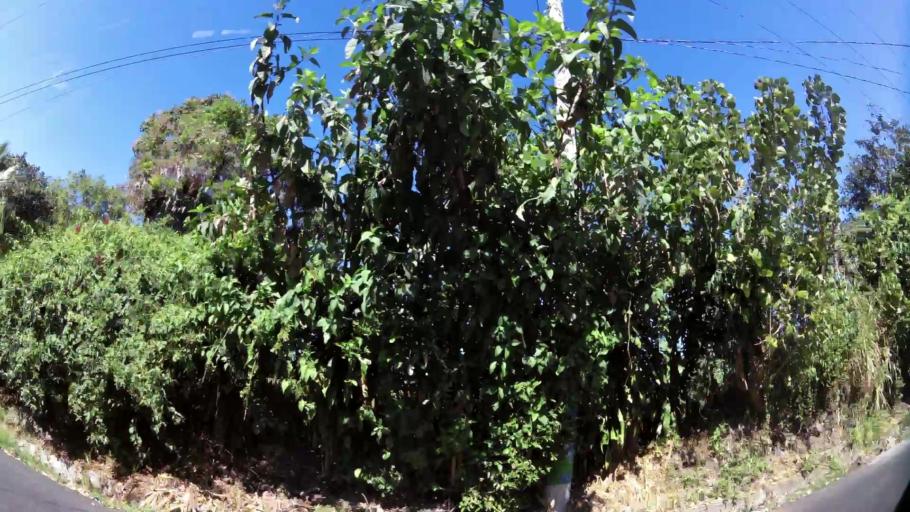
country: SV
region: La Libertad
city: Santa Tecla
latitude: 13.7325
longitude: -89.3750
